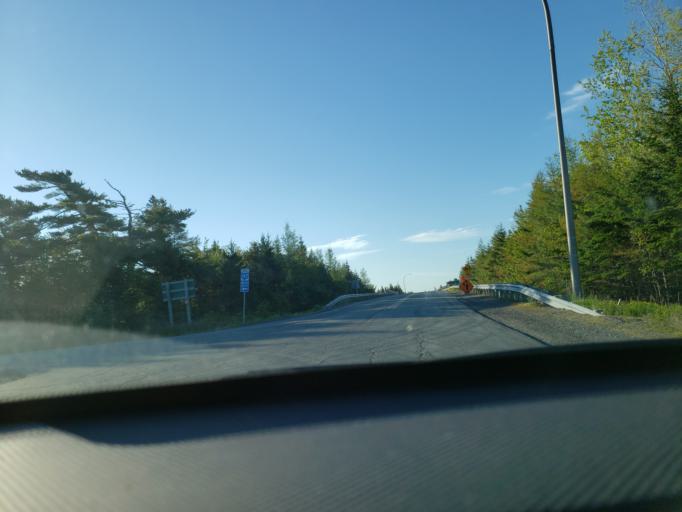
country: CA
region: Nova Scotia
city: Cole Harbour
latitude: 44.7139
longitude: -63.3950
